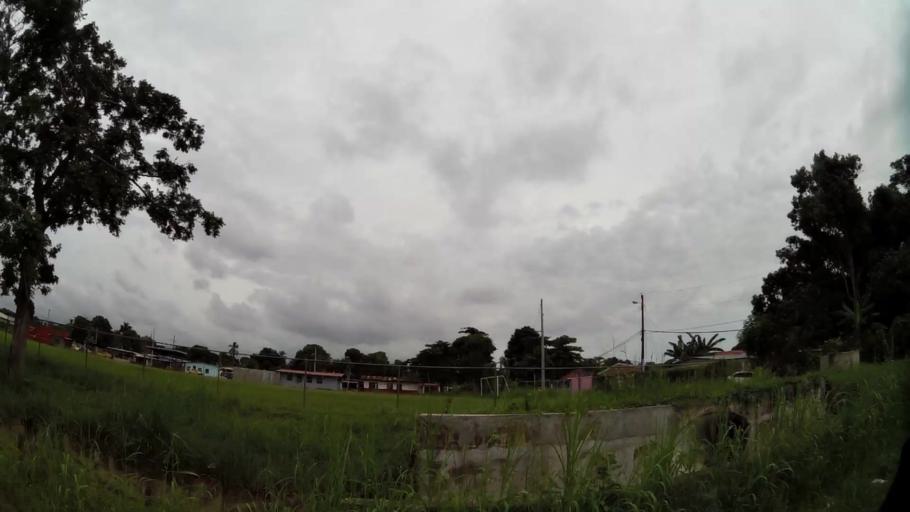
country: PA
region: Panama
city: San Miguelito
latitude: 9.0476
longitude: -79.4286
